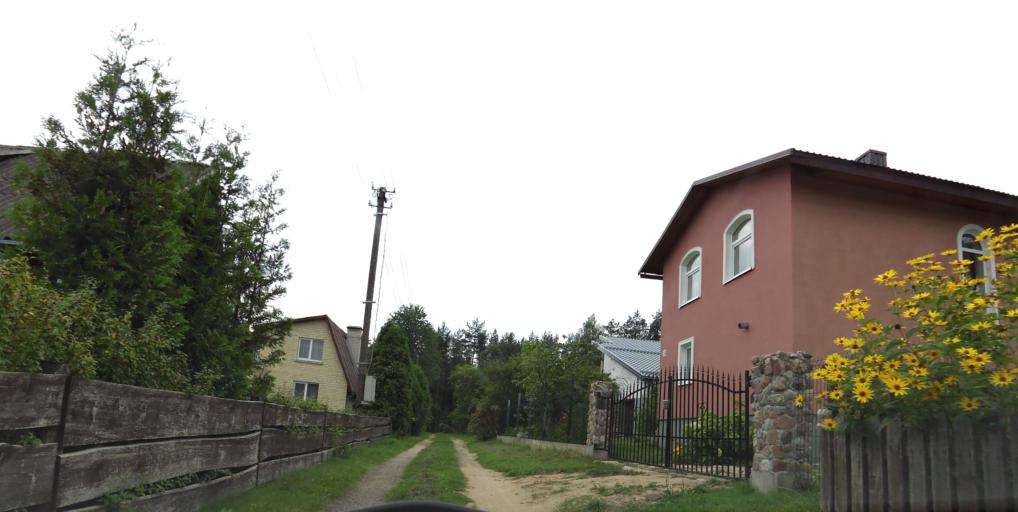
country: LT
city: Grigiskes
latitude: 54.7549
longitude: 25.0122
